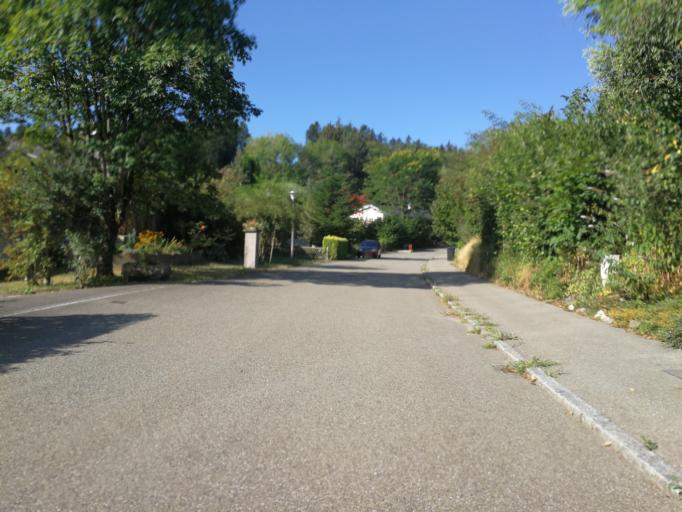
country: CH
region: Zurich
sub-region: Bezirk Uster
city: Esslingen
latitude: 47.2831
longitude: 8.7119
